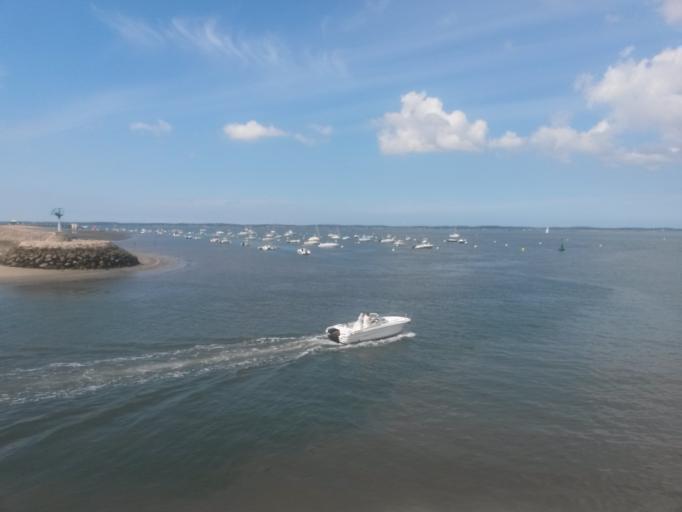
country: FR
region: Aquitaine
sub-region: Departement de la Gironde
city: Arcachon
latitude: 44.6627
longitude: -1.1511
